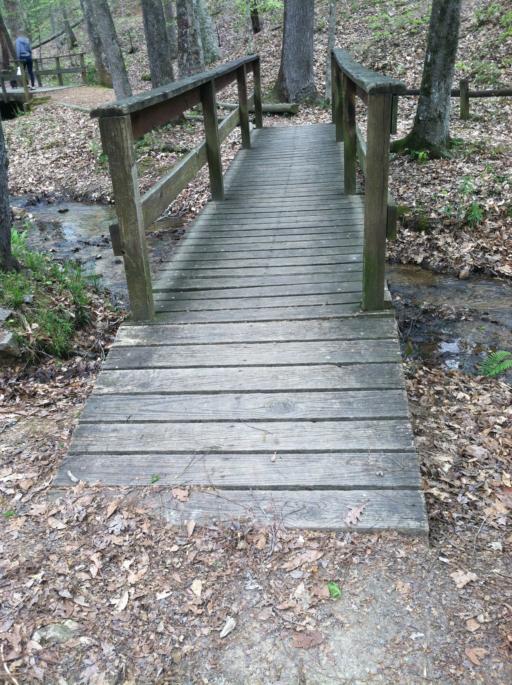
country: US
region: Georgia
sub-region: Harris County
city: Pine Mountain
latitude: 32.8429
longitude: -84.8273
